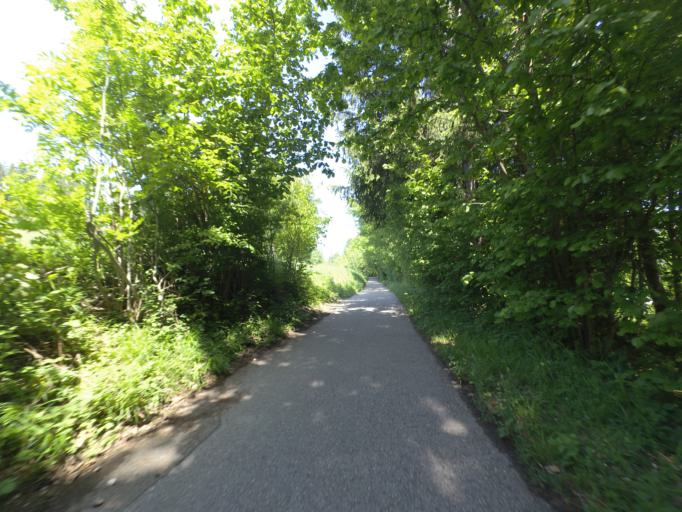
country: DE
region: Bavaria
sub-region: Upper Bavaria
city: Petting
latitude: 47.9311
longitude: 12.7777
